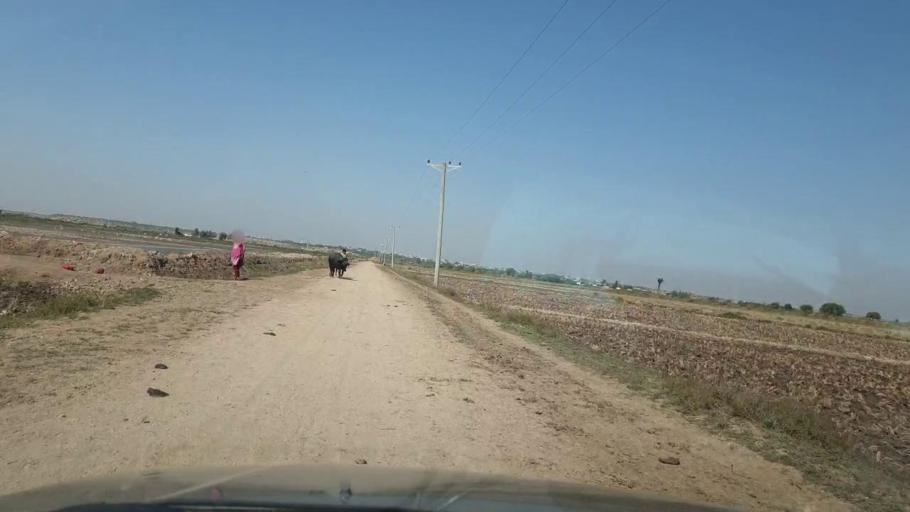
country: PK
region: Sindh
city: Thatta
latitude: 24.7202
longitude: 67.9182
